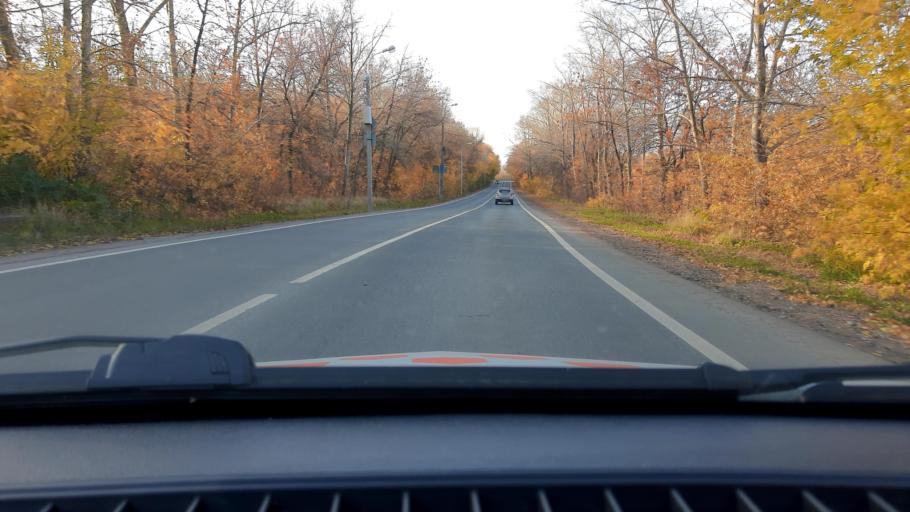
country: RU
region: Bashkortostan
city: Ufa
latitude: 54.8596
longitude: 56.0762
